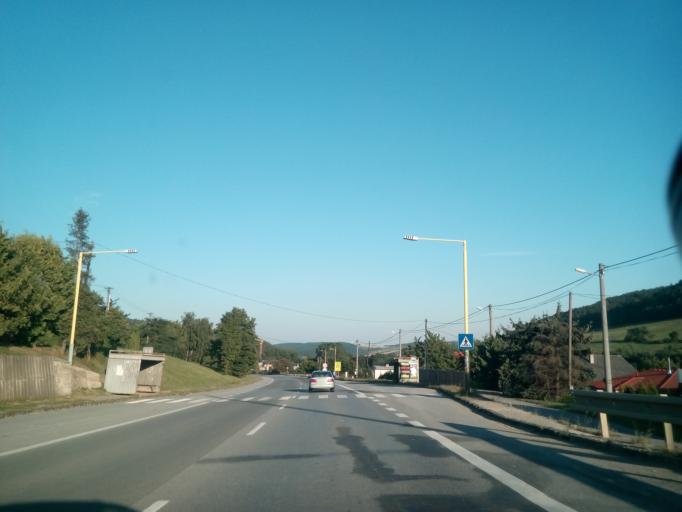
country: SK
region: Presovsky
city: Sabinov
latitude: 49.0222
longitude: 21.0261
